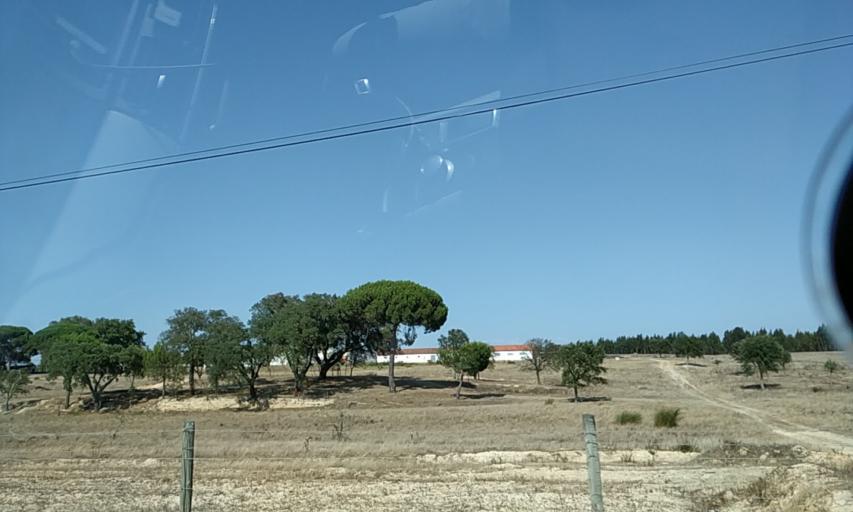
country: PT
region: Evora
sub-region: Vendas Novas
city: Vendas Novas
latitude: 38.7334
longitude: -8.6244
